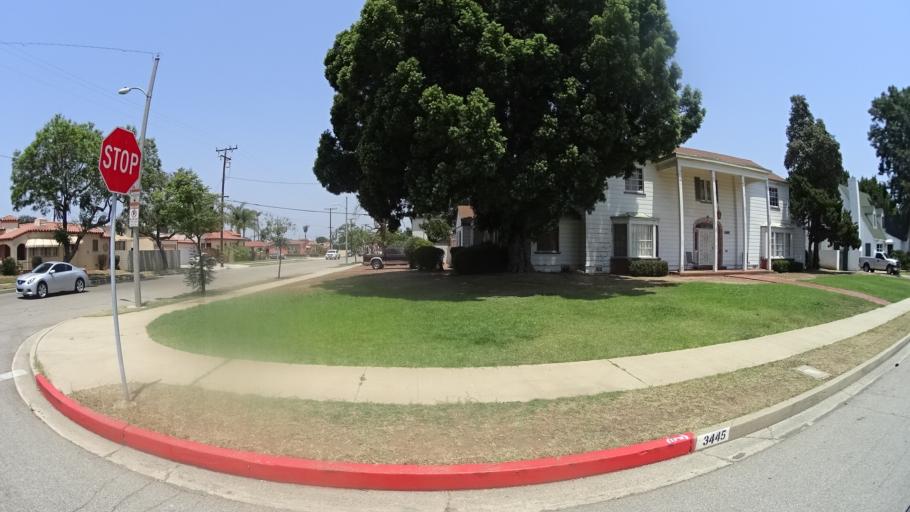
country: US
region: California
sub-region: Los Angeles County
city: Inglewood
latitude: 33.9655
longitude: -118.3329
